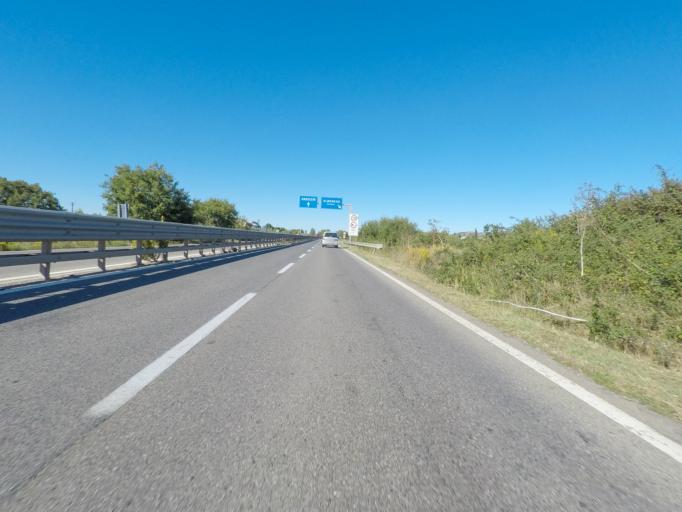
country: IT
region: Tuscany
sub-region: Provincia di Grosseto
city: Grosseto
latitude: 42.6995
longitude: 11.1376
